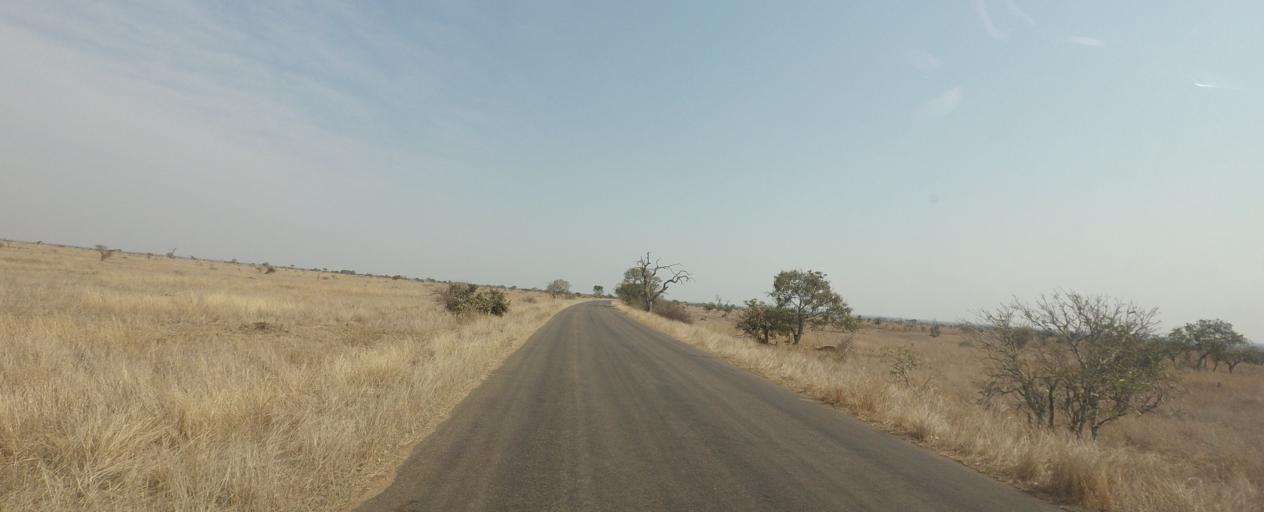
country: ZA
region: Limpopo
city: Thulamahashi
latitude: -24.3232
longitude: 31.7519
